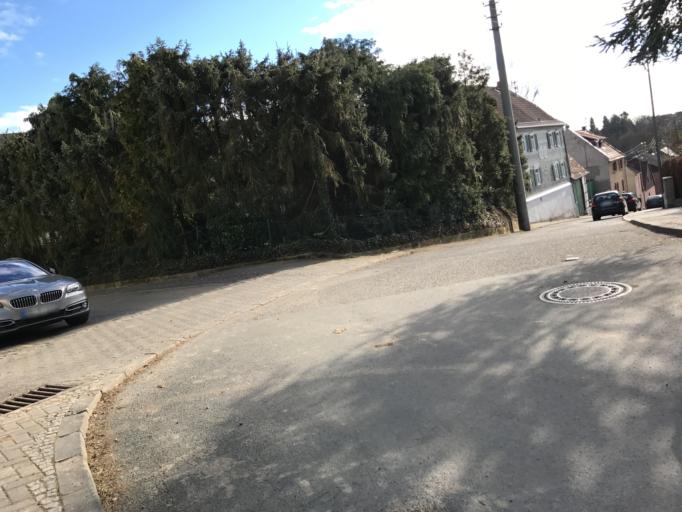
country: DE
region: Hesse
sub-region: Regierungsbezirk Darmstadt
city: Niedernhausen
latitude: 50.0965
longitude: 8.3066
